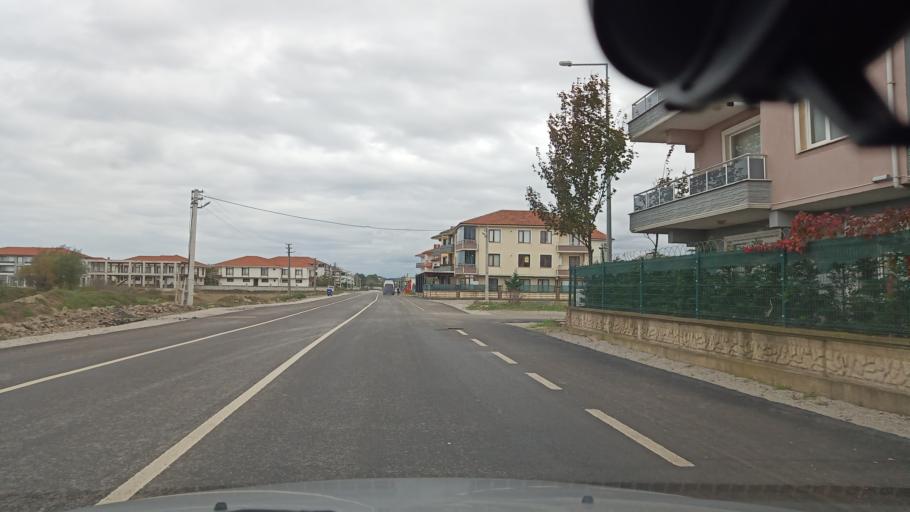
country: TR
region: Sakarya
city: Karasu
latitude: 41.1151
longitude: 30.6701
